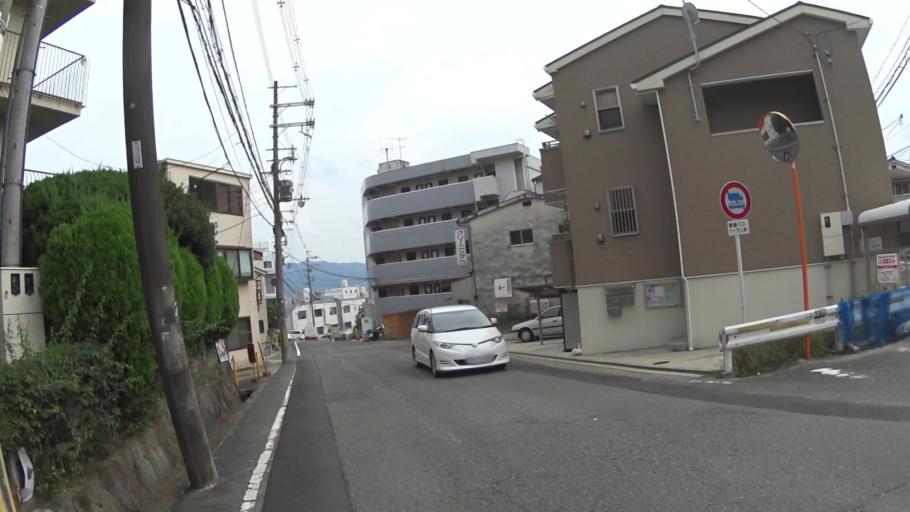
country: JP
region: Kyoto
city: Kyoto
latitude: 34.9845
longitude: 135.7990
